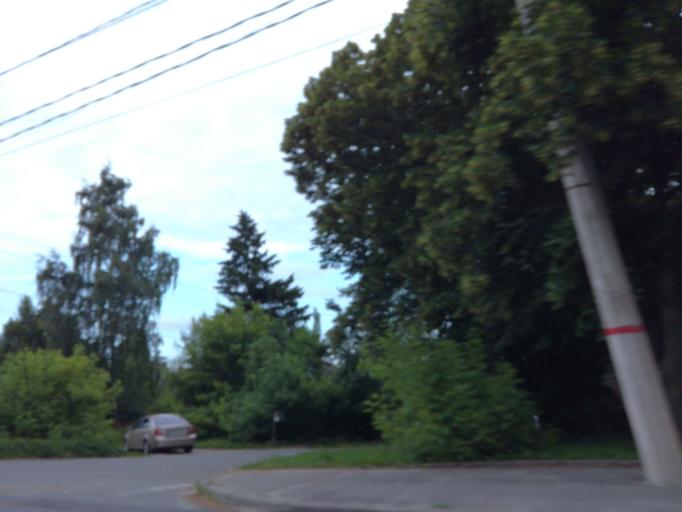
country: RU
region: Kursk
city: Kursk
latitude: 51.7615
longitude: 36.1645
